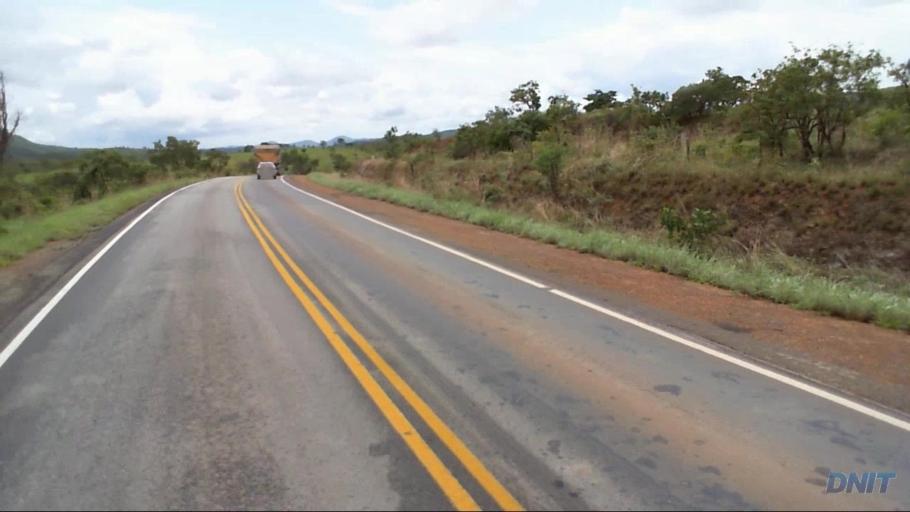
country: BR
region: Goias
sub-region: Padre Bernardo
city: Padre Bernardo
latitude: -15.4670
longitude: -48.2277
